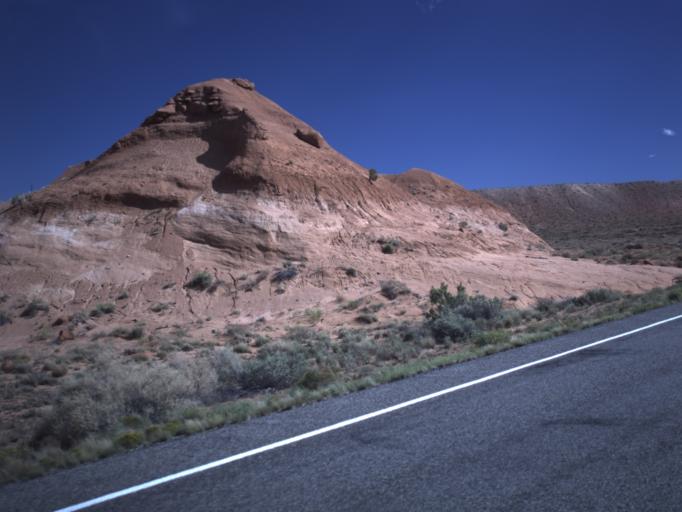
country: US
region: Utah
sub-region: Emery County
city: Ferron
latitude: 38.3126
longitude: -110.6729
